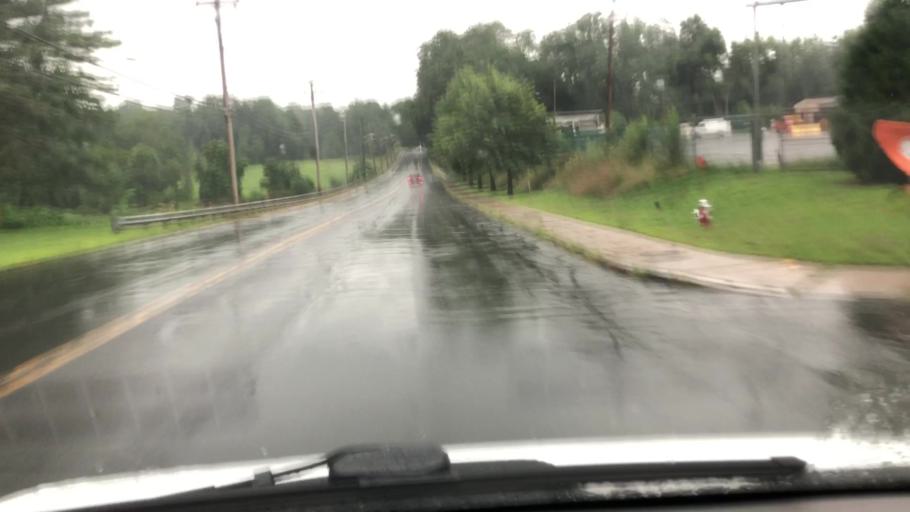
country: US
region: Massachusetts
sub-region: Hampshire County
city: Northampton
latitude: 42.3328
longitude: -72.6567
